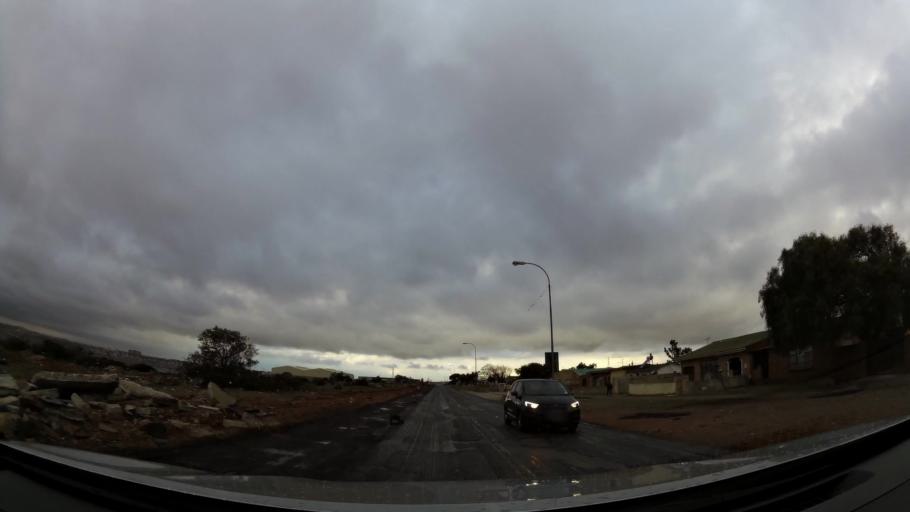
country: ZA
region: Eastern Cape
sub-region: Nelson Mandela Bay Metropolitan Municipality
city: Port Elizabeth
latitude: -33.8955
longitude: 25.5421
